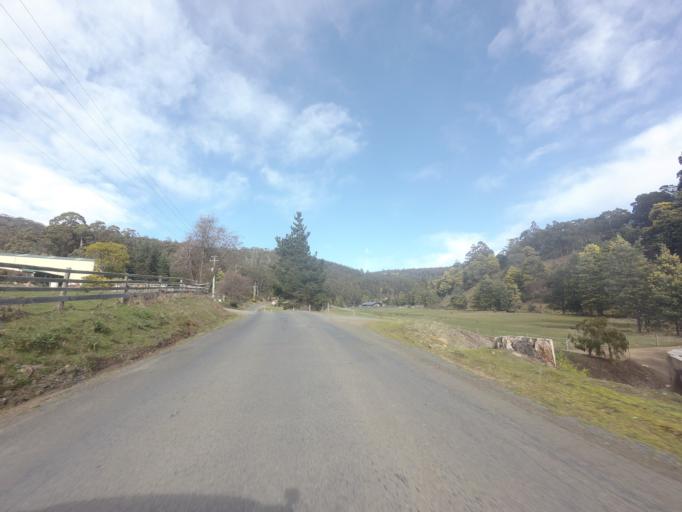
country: AU
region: Tasmania
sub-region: Kingborough
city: Margate
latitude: -42.9985
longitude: 147.1780
